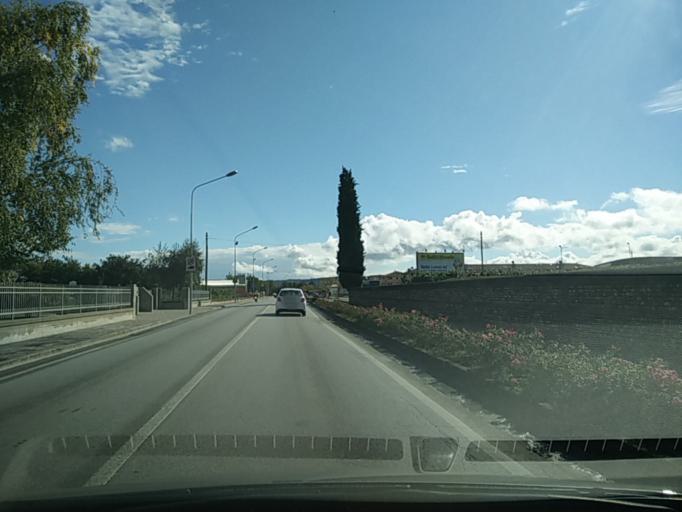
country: IT
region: Veneto
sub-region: Provincia di Treviso
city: Vidor
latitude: 45.8605
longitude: 12.0424
